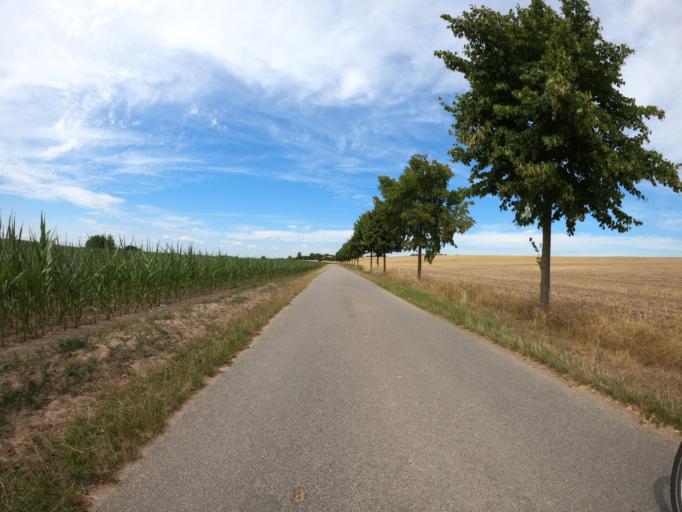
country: DE
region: Mecklenburg-Vorpommern
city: Woldegk
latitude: 53.4526
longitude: 13.4972
